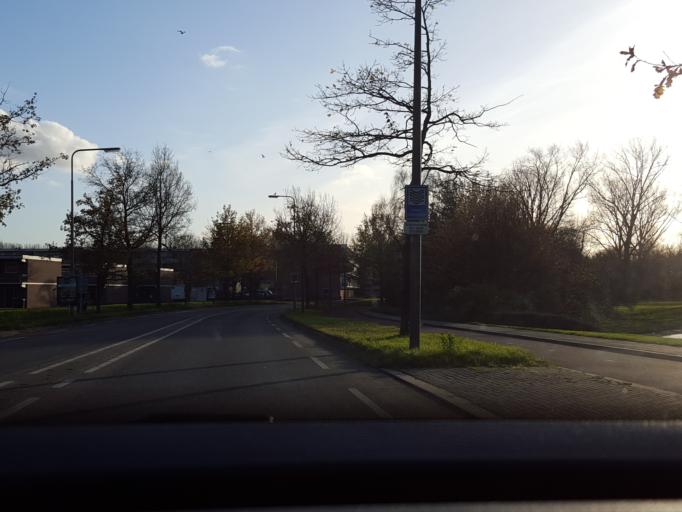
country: NL
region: Gelderland
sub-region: Gemeente Zutphen
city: Zutphen
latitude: 52.1349
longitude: 6.1989
